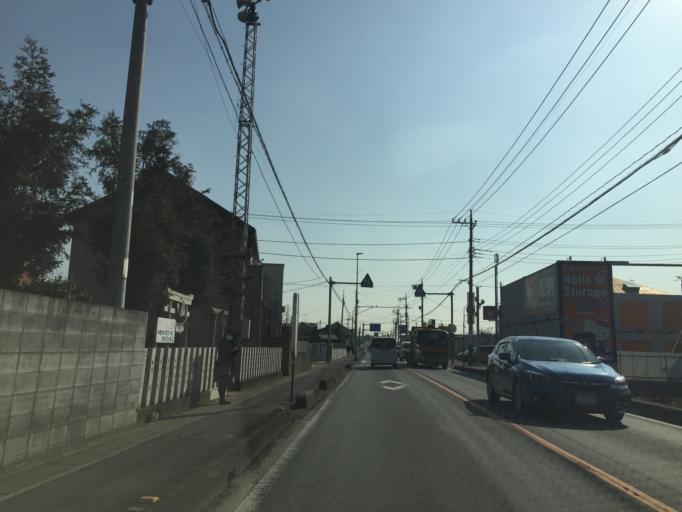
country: JP
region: Saitama
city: Shiki
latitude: 35.8356
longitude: 139.5976
